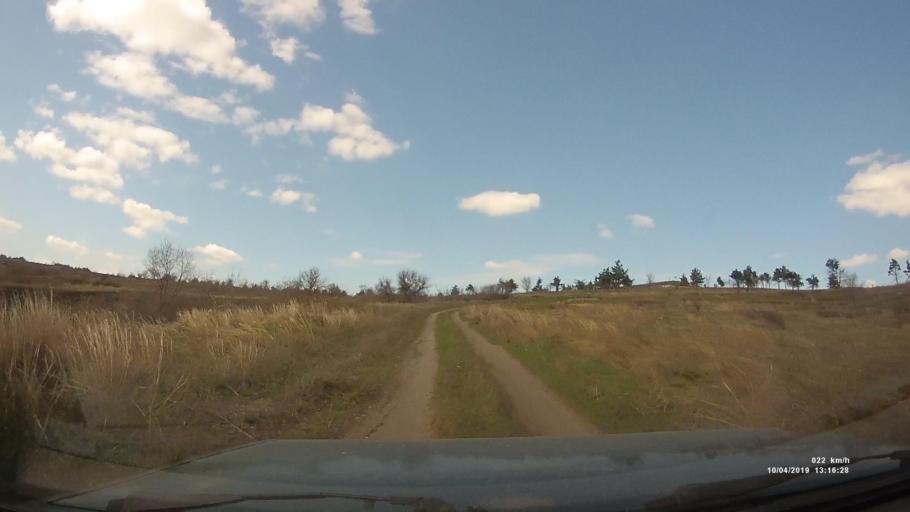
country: RU
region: Rostov
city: Masalovka
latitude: 48.4209
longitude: 40.2559
